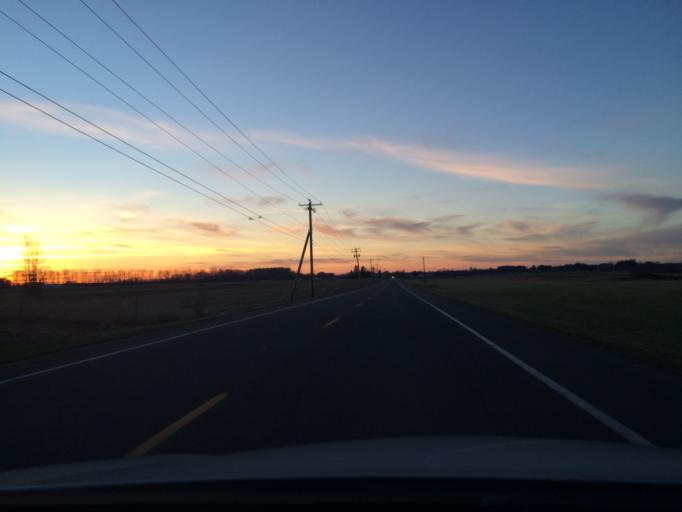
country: US
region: Washington
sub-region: Whatcom County
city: Everson
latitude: 48.9420
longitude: -122.3945
